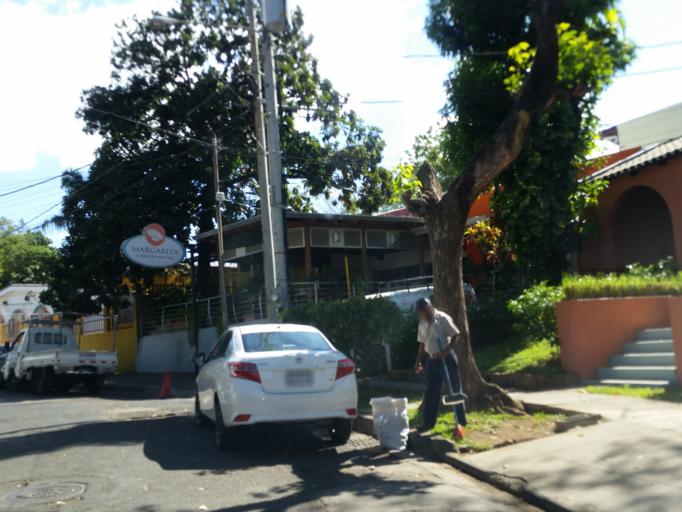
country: NI
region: Managua
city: Managua
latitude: 12.1214
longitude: -86.2595
